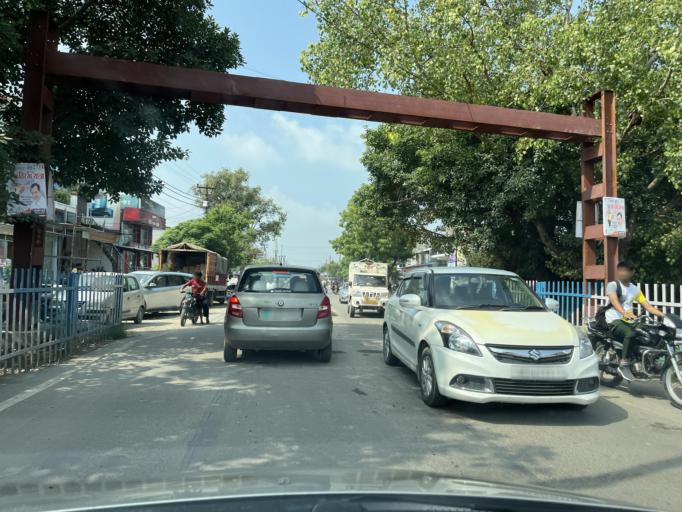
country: IN
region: Uttarakhand
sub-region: Udham Singh Nagar
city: Bazpur
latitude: 29.1575
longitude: 79.1495
